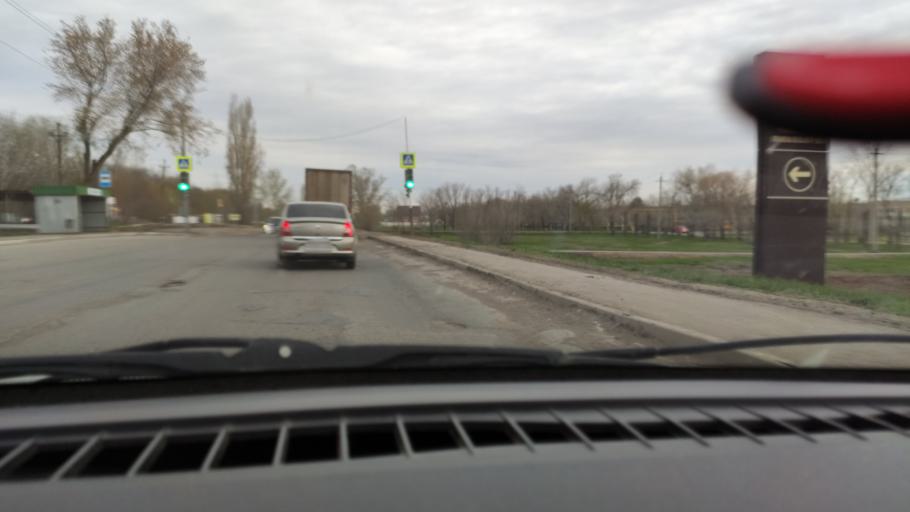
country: RU
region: Orenburg
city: Tatarskaya Kargala
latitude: 51.8662
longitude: 55.1403
